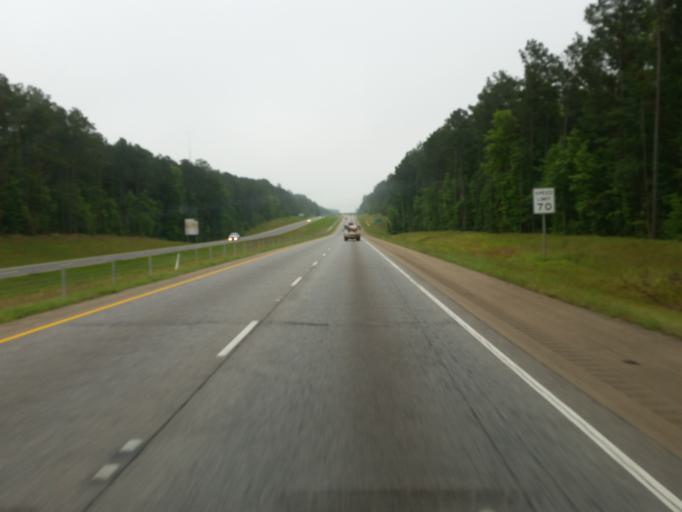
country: US
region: Louisiana
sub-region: Webster Parish
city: Minden
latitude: 32.5785
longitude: -93.2390
